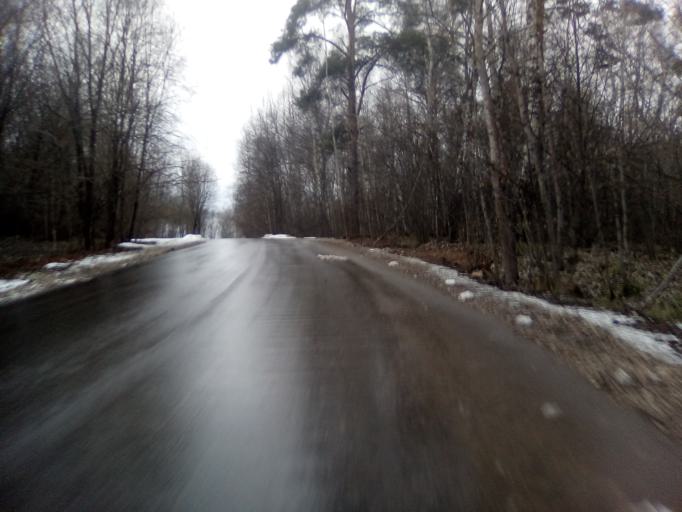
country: RU
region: Moskovskaya
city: Dubrovitsy
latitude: 55.5021
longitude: 37.4307
